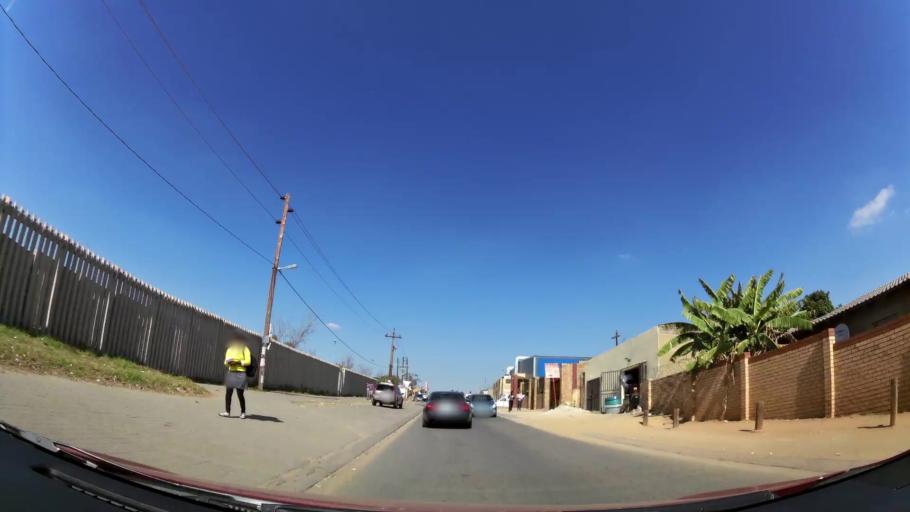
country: ZA
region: Gauteng
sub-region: West Rand District Municipality
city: Muldersdriseloop
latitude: -26.0165
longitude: 27.9371
